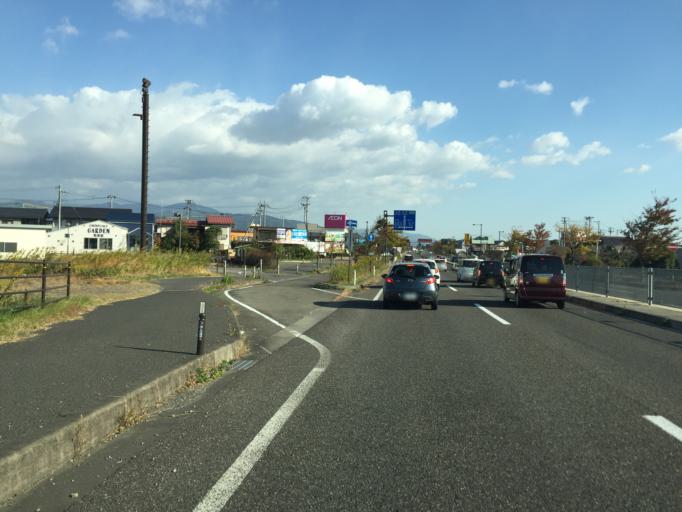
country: JP
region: Fukushima
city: Fukushima-shi
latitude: 37.7832
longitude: 140.4548
